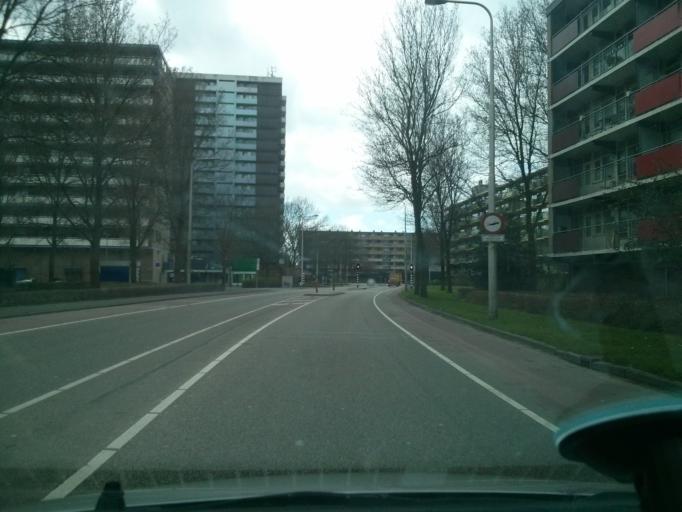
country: NL
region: North Holland
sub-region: Gemeente Amstelveen
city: Amstelveen
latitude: 52.2906
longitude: 4.8691
